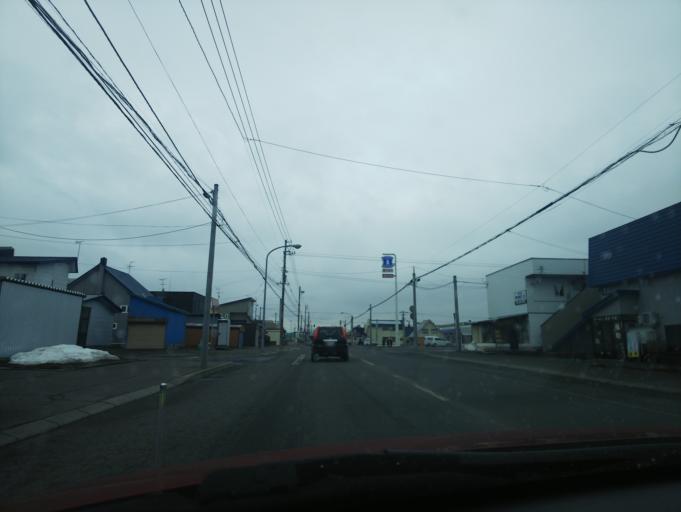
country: JP
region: Hokkaido
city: Nayoro
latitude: 44.3508
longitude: 142.4503
